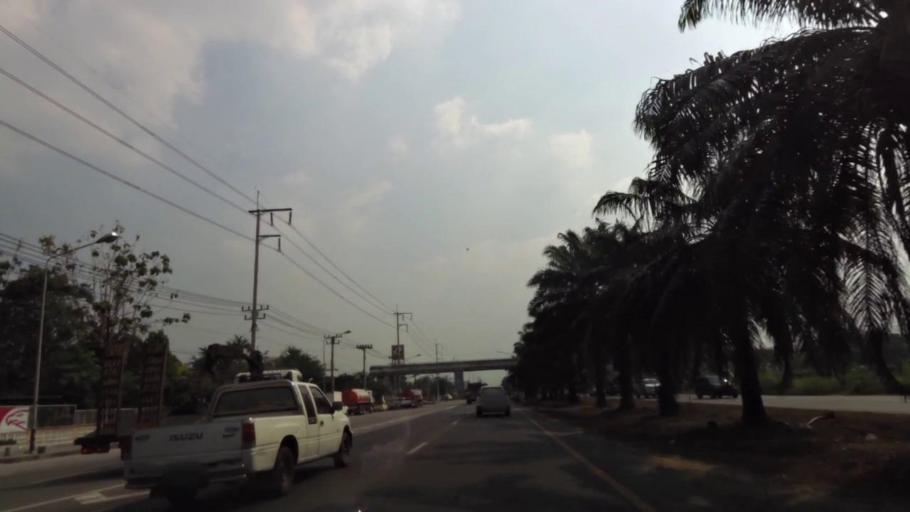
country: TH
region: Chon Buri
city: Ban Bueng
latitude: 13.3137
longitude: 101.1056
